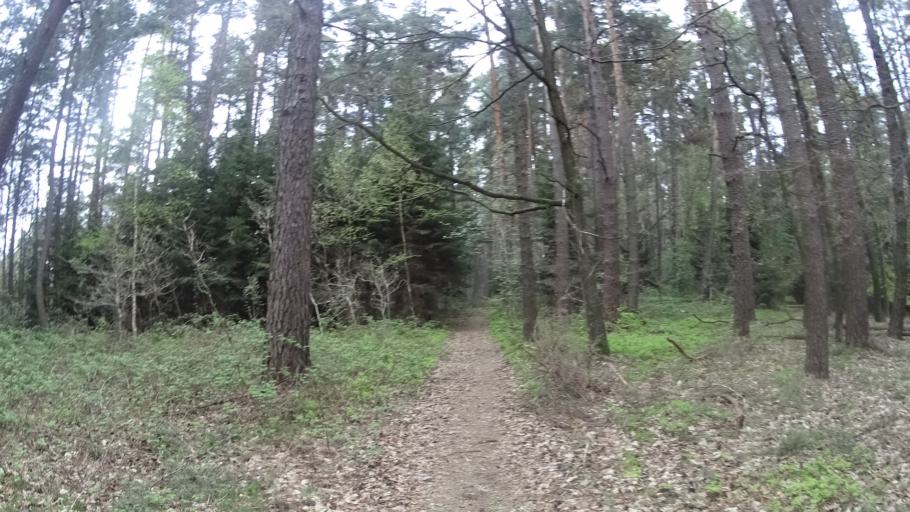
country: DE
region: Bavaria
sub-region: Upper Franconia
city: Kleinsendelbach
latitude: 49.6183
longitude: 11.1805
